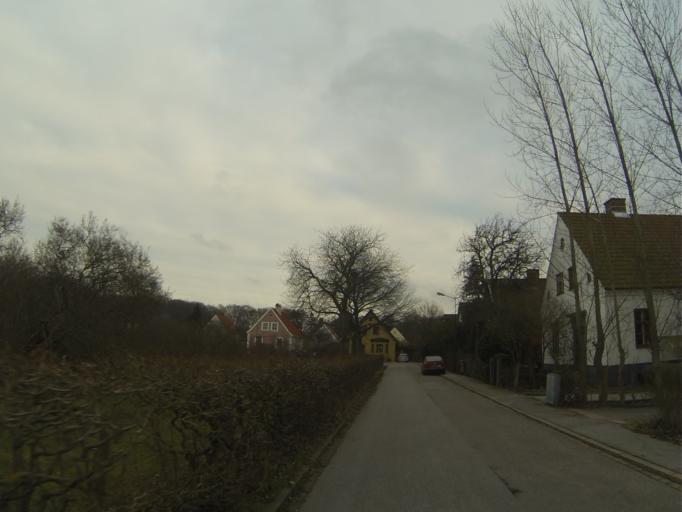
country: SE
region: Skane
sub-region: Burlovs Kommun
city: Arloev
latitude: 55.6122
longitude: 13.0451
